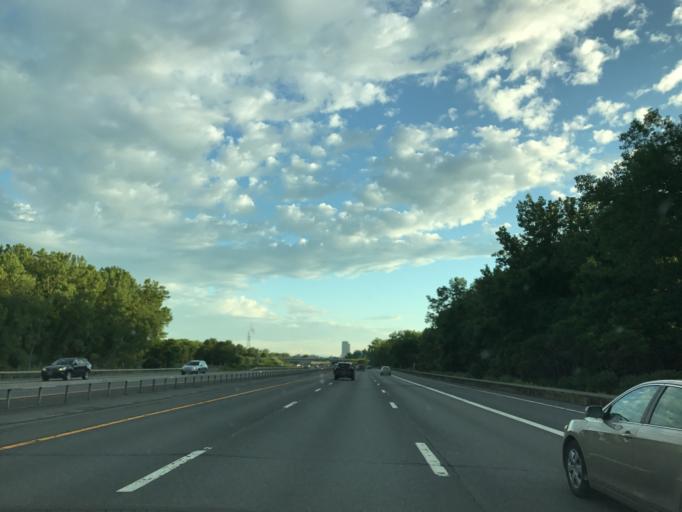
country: US
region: New York
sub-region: Albany County
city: Menands
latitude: 42.6873
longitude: -73.7176
